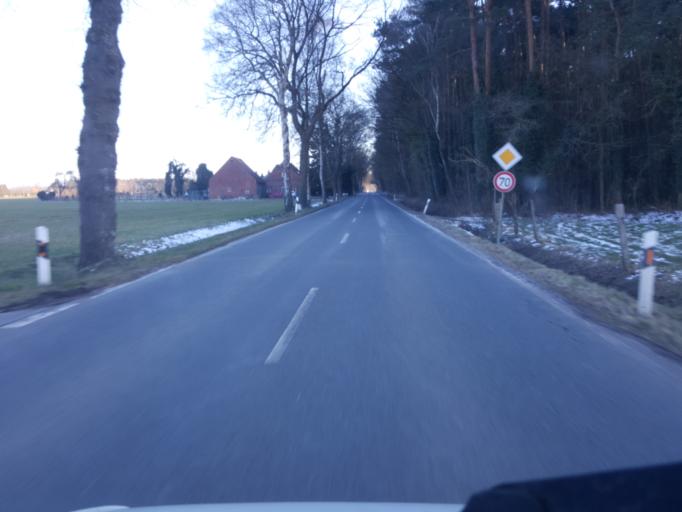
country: DE
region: North Rhine-Westphalia
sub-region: Regierungsbezirk Detmold
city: Hille
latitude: 52.3754
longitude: 8.7268
